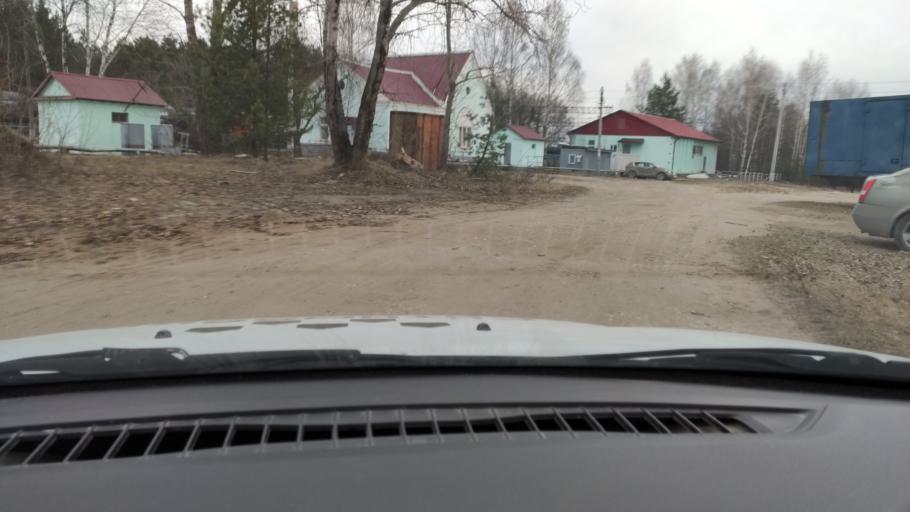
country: RU
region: Perm
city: Perm
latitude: 58.0453
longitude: 56.2058
